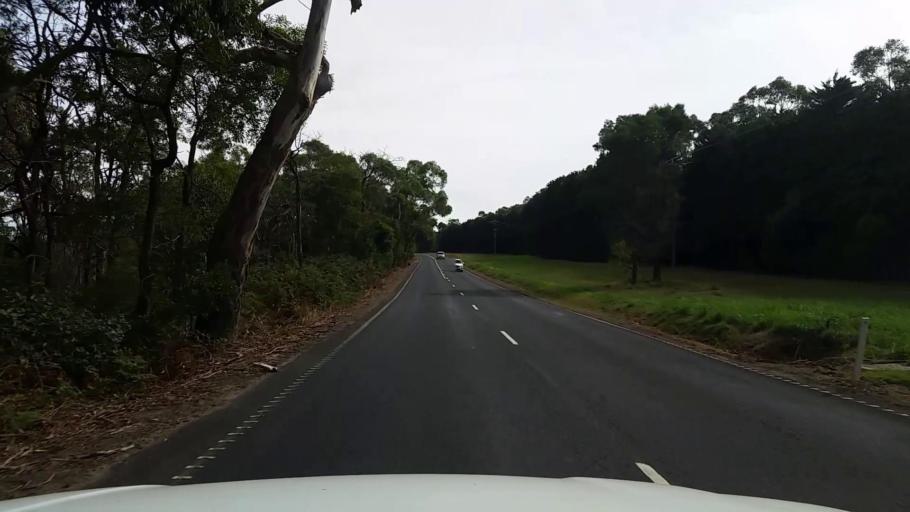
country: AU
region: Victoria
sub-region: Mornington Peninsula
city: Mount Martha
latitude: -38.3061
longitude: 145.0826
